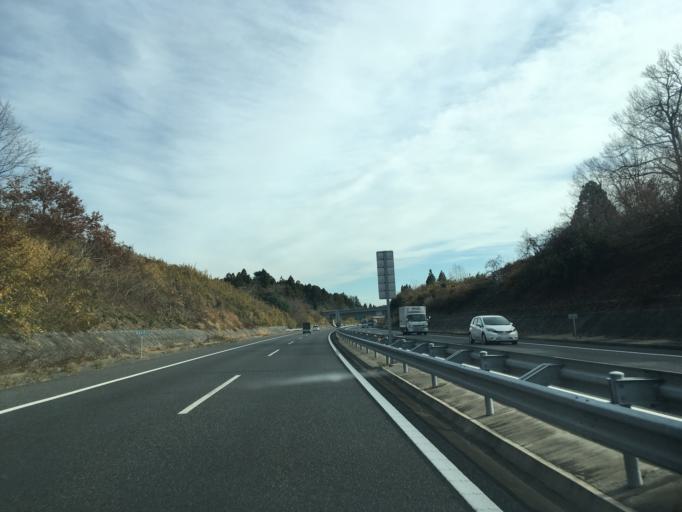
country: JP
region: Ibaraki
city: Ami
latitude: 35.9801
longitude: 140.2497
